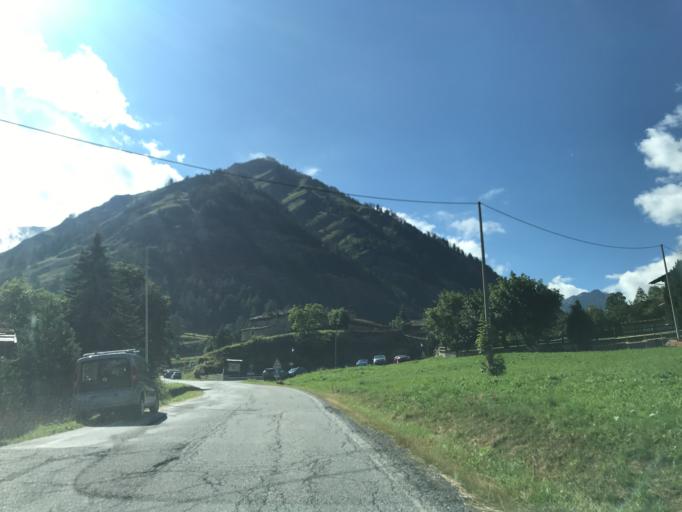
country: IT
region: Piedmont
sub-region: Provincia di Cuneo
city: Pontechianale
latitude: 44.6245
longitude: 7.0267
